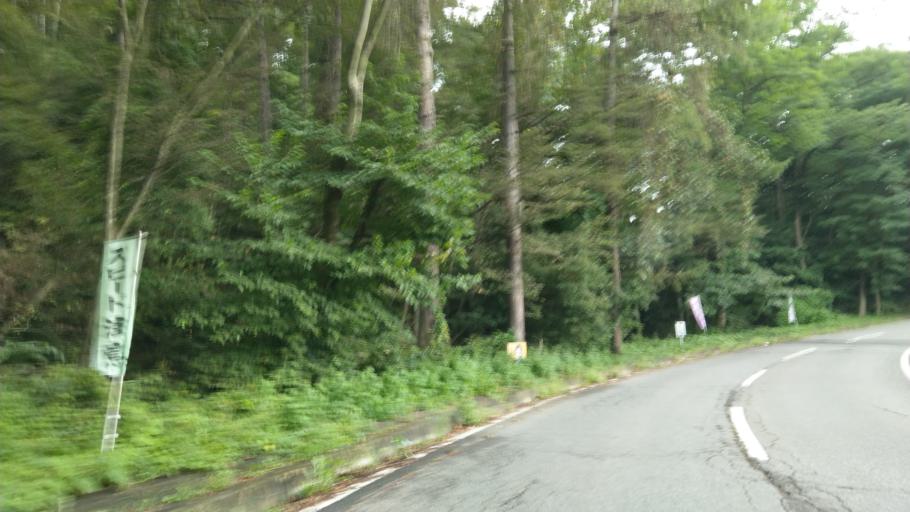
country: JP
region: Nagano
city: Komoro
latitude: 36.3271
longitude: 138.3996
